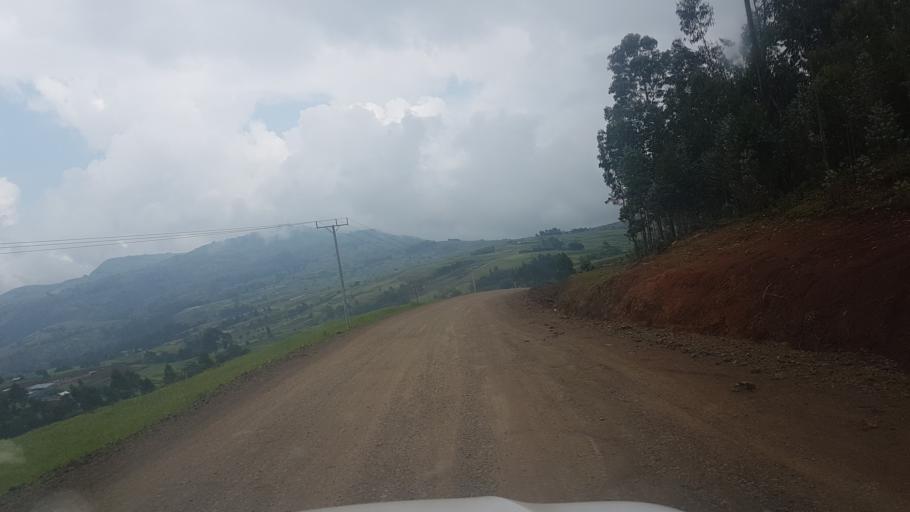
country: ET
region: Southern Nations, Nationalities, and People's Region
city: Arba Minch'
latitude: 6.3231
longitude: 37.5483
